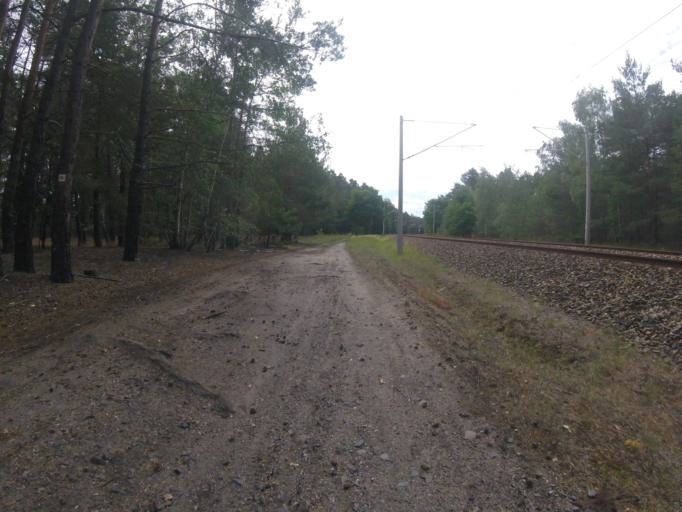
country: DE
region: Brandenburg
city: Bestensee
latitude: 52.2054
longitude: 13.6223
